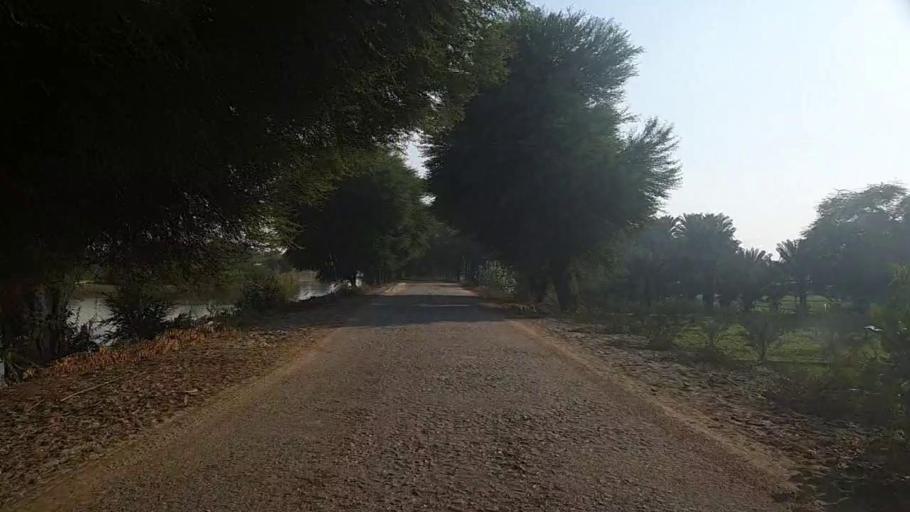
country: PK
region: Sindh
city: Bozdar
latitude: 27.2556
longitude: 68.6765
